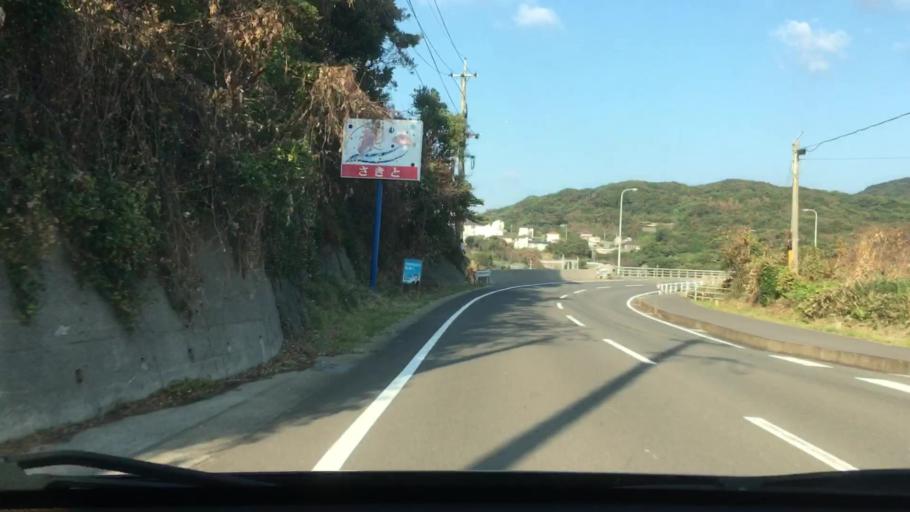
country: JP
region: Nagasaki
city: Sasebo
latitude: 33.0281
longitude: 129.5845
